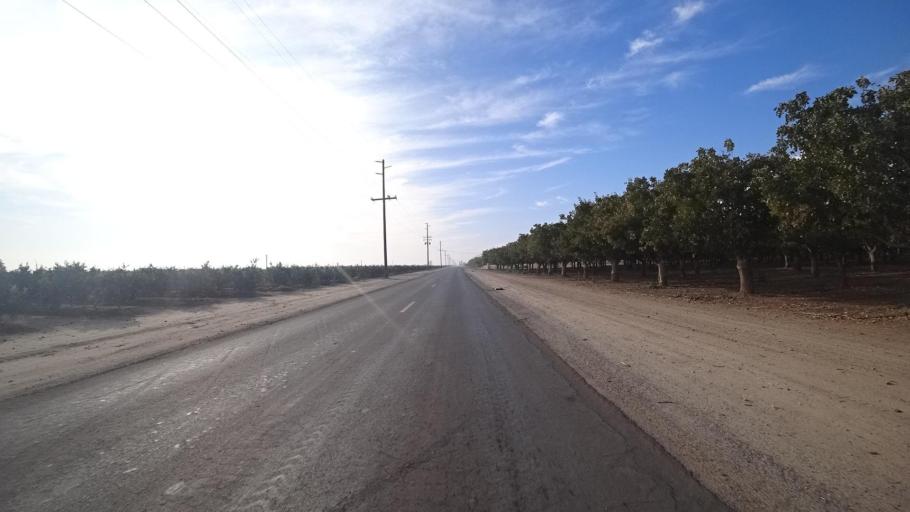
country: US
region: California
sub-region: Kern County
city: Delano
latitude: 35.7732
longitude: -119.2053
